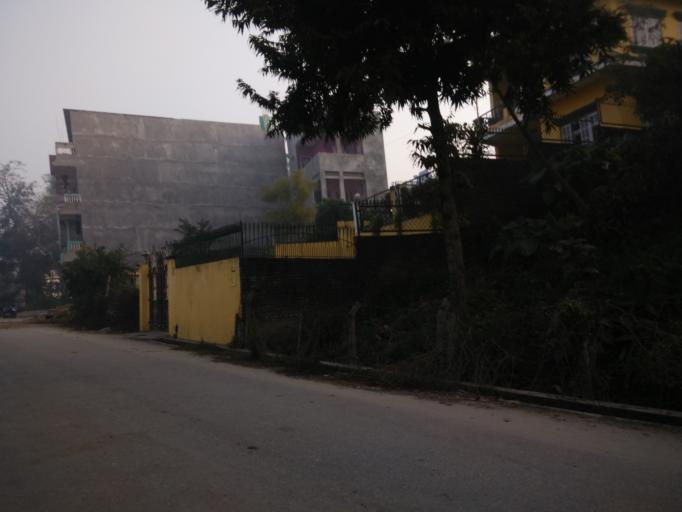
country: NP
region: Central Region
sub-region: Narayani Zone
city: Bharatpur
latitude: 27.6930
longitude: 84.4266
